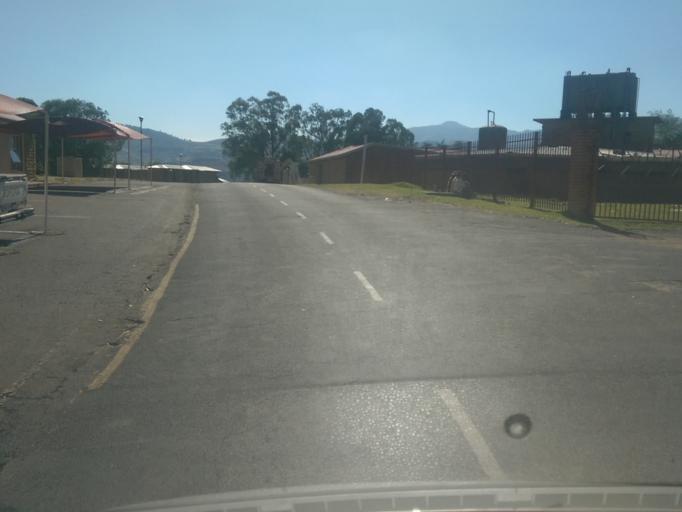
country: LS
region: Maseru
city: Nako
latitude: -29.4520
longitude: 27.7225
